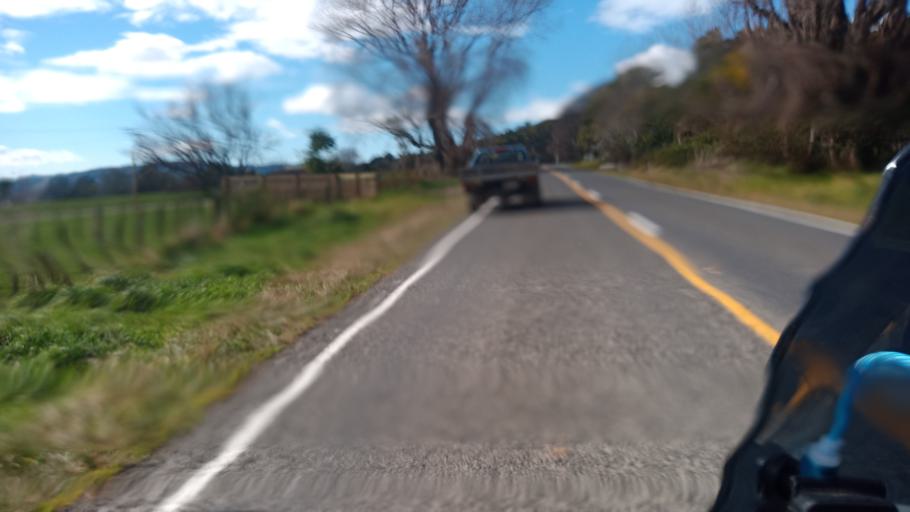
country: NZ
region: Gisborne
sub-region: Gisborne District
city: Gisborne
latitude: -37.9068
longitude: 178.2897
